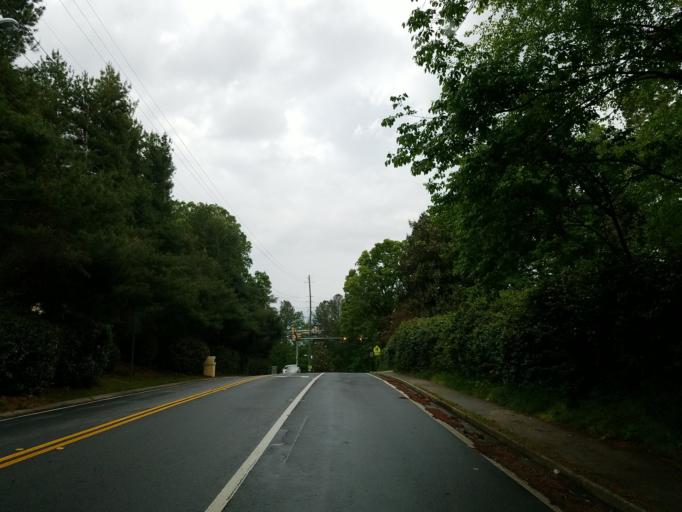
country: US
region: Georgia
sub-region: Fulton County
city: Roswell
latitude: 33.9928
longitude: -84.4438
